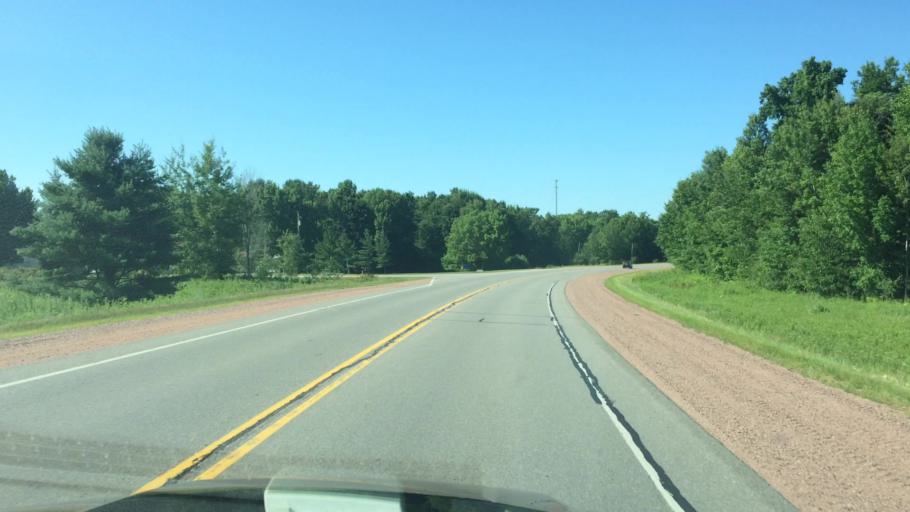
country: US
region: Wisconsin
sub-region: Marathon County
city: Stratford
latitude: 44.7367
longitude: -90.0797
